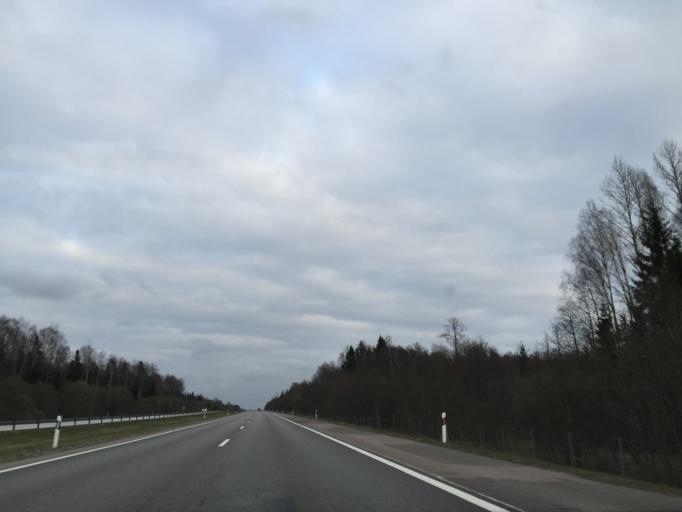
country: LT
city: Rietavas
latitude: 55.6343
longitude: 21.9270
